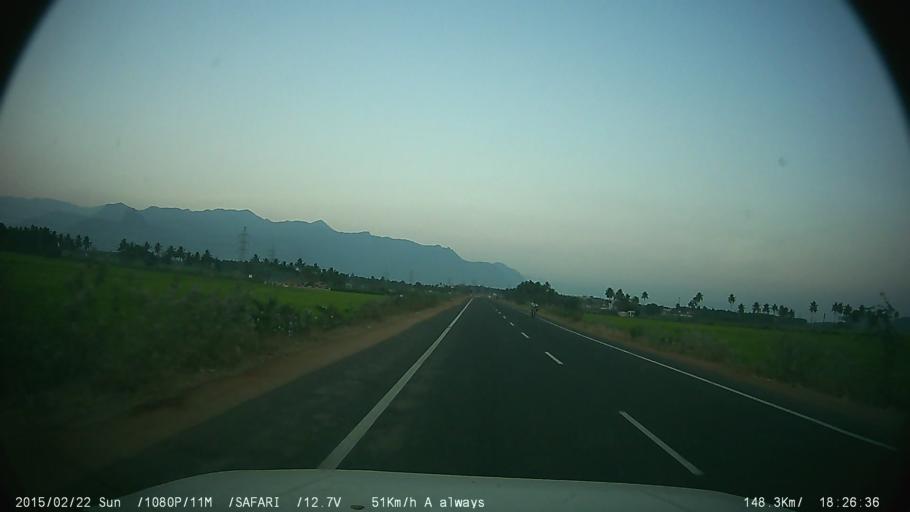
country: IN
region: Tamil Nadu
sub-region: Theni
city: Teni
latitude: 9.9649
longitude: 77.4400
